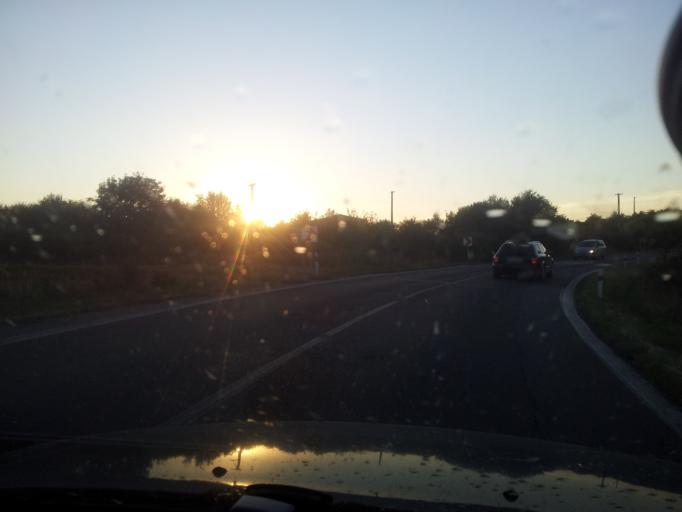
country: SK
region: Nitriansky
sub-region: Okres Nove Zamky
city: Sturovo
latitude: 47.8828
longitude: 18.6414
